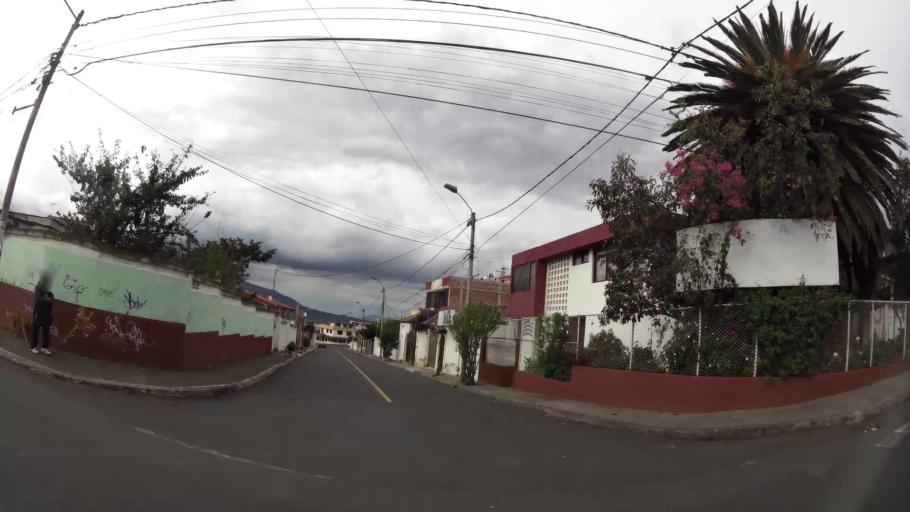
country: EC
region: Tungurahua
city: Ambato
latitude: -1.2731
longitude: -78.6277
